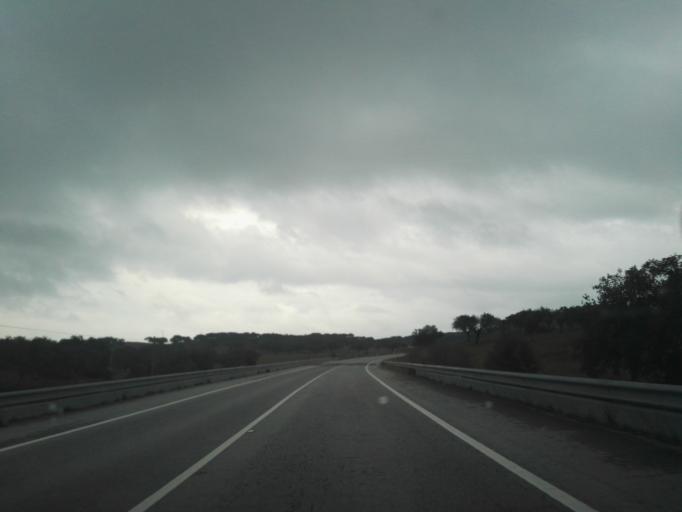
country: PT
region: Portalegre
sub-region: Portalegre
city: Alegrete
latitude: 39.1799
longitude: -7.3427
